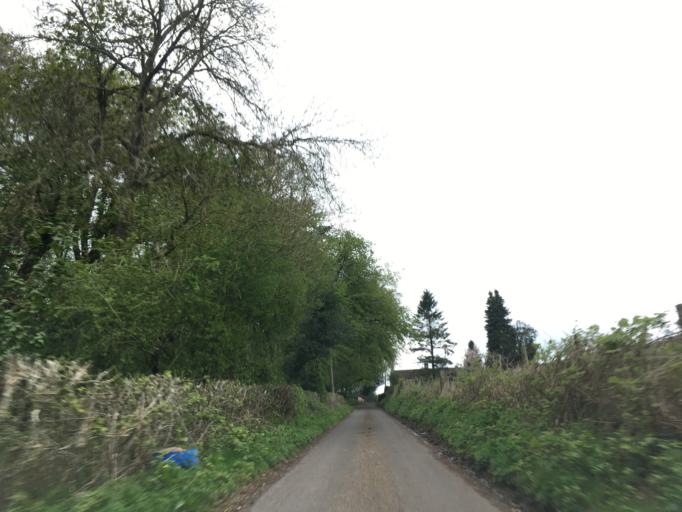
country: GB
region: England
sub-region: Gloucestershire
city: Wotton-under-Edge
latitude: 51.6430
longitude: -2.3044
